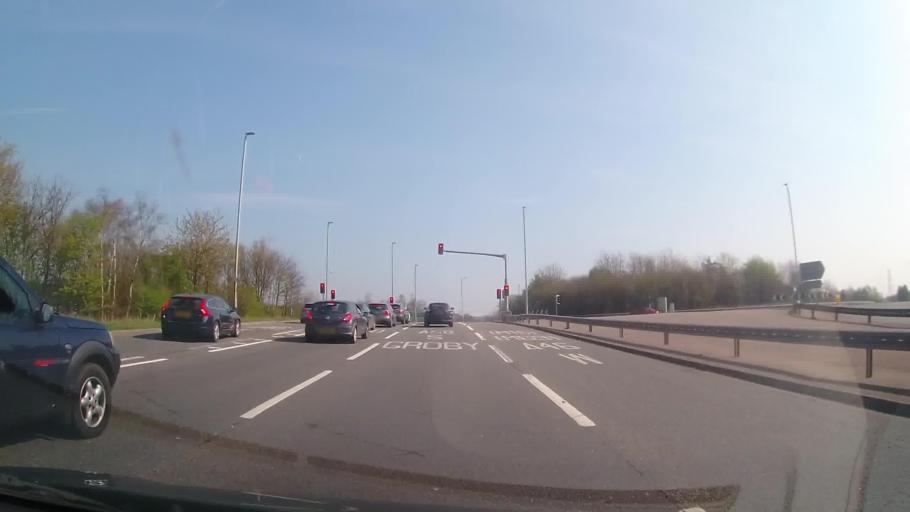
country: GB
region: England
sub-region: Leicestershire
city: Glenfield
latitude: 52.6626
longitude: -1.2065
